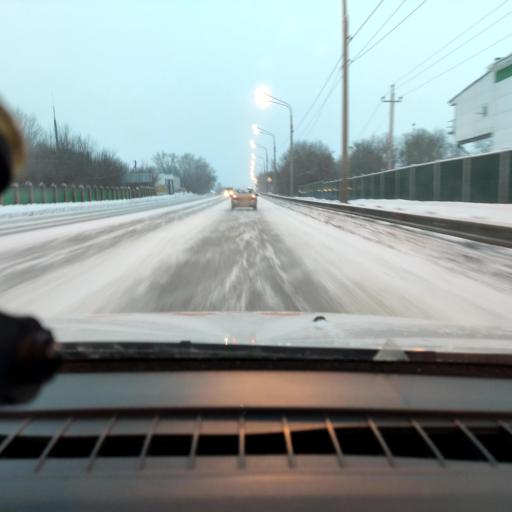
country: RU
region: Samara
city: Otradnyy
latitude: 53.3620
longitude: 51.3501
